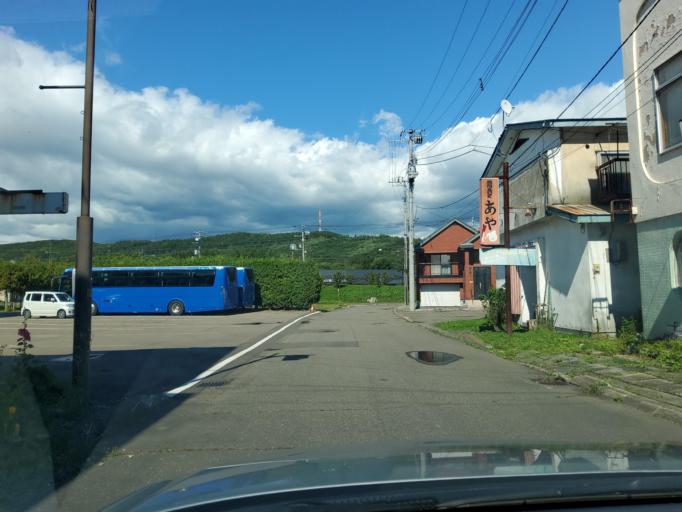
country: JP
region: Hokkaido
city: Obihiro
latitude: 42.9322
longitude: 143.3002
